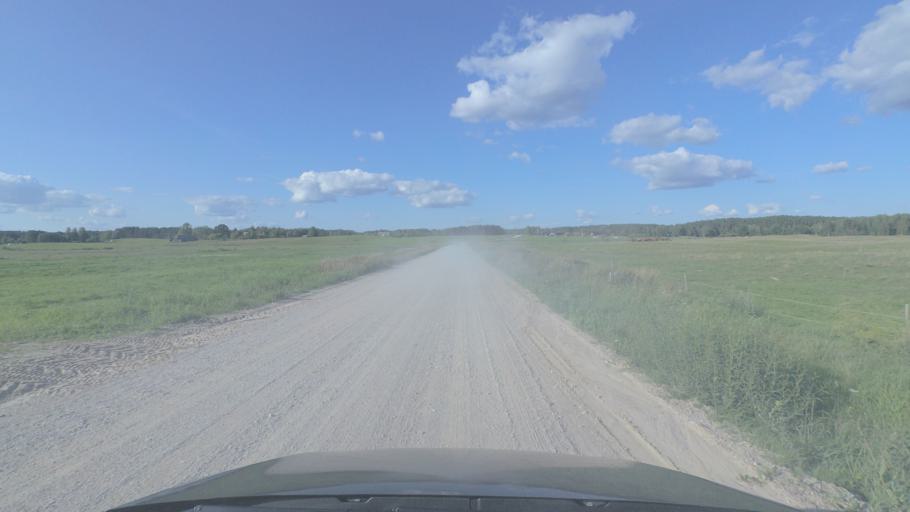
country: LT
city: Pabrade
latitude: 55.1330
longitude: 25.7070
